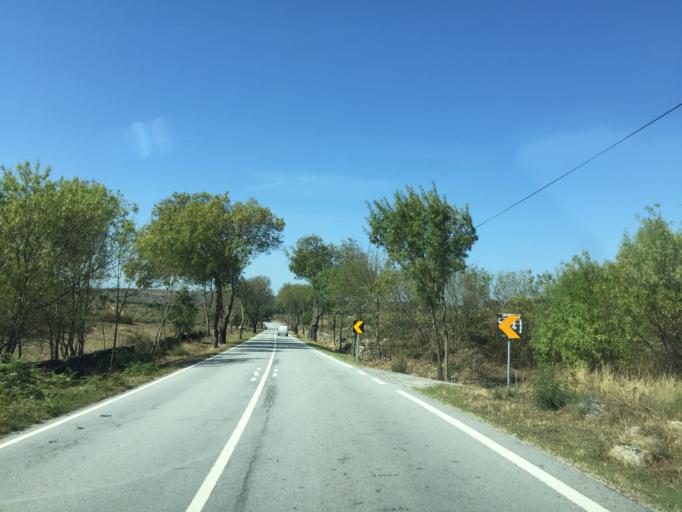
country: PT
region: Portalegre
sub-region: Castelo de Vide
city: Castelo de Vide
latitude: 39.4357
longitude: -7.5142
